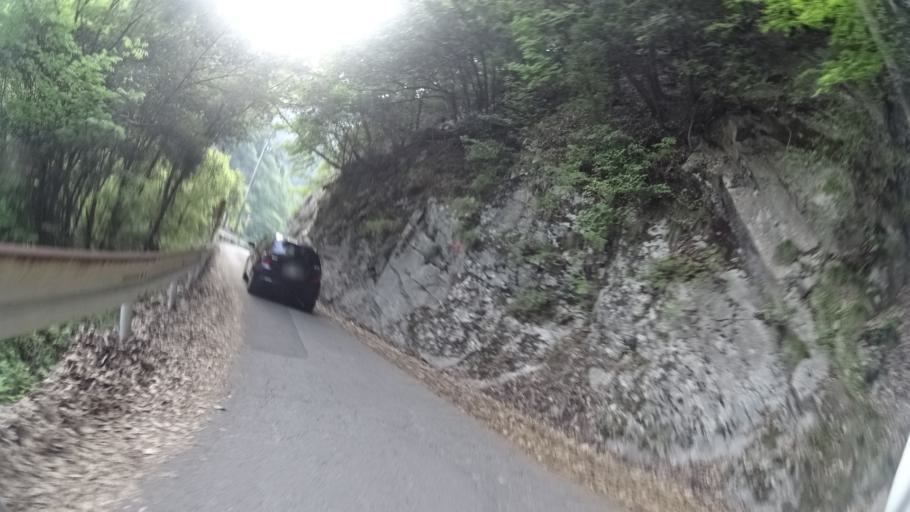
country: JP
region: Tokushima
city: Ikedacho
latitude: 33.9025
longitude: 133.8145
